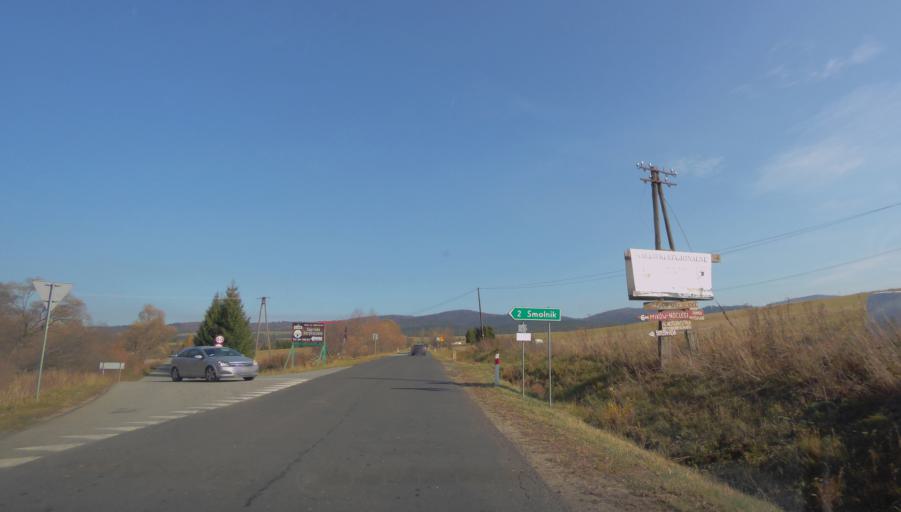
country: PL
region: Subcarpathian Voivodeship
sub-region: Powiat sanocki
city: Komancza
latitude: 49.2463
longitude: 22.1167
